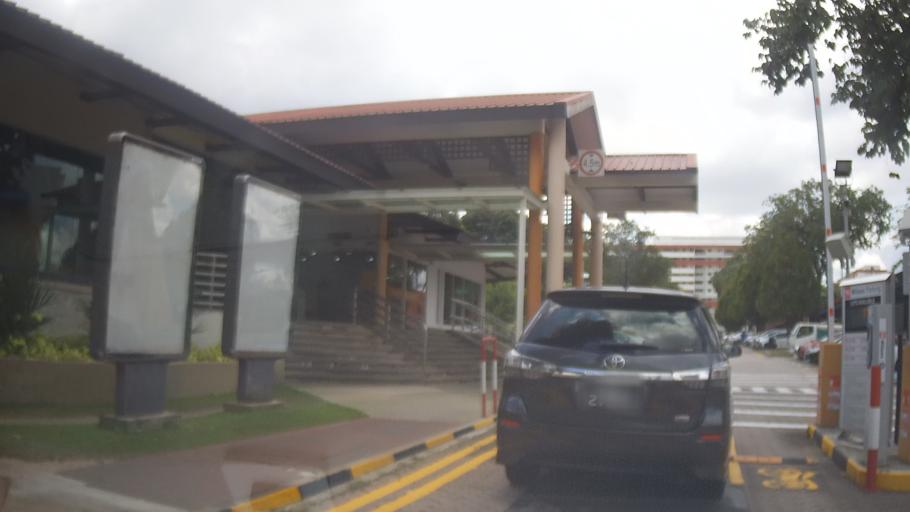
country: MY
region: Johor
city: Johor Bahru
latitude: 1.4342
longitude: 103.7792
